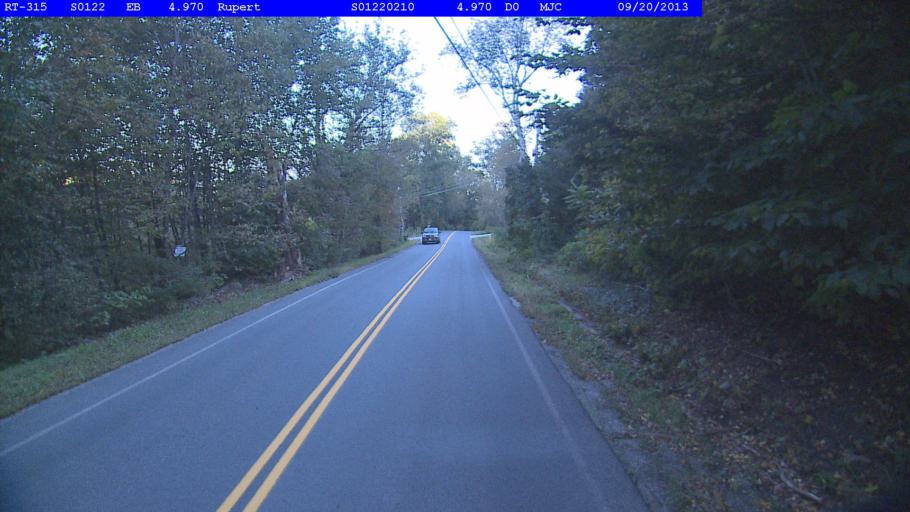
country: US
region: Vermont
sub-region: Bennington County
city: Manchester Center
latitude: 43.2789
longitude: -73.1389
